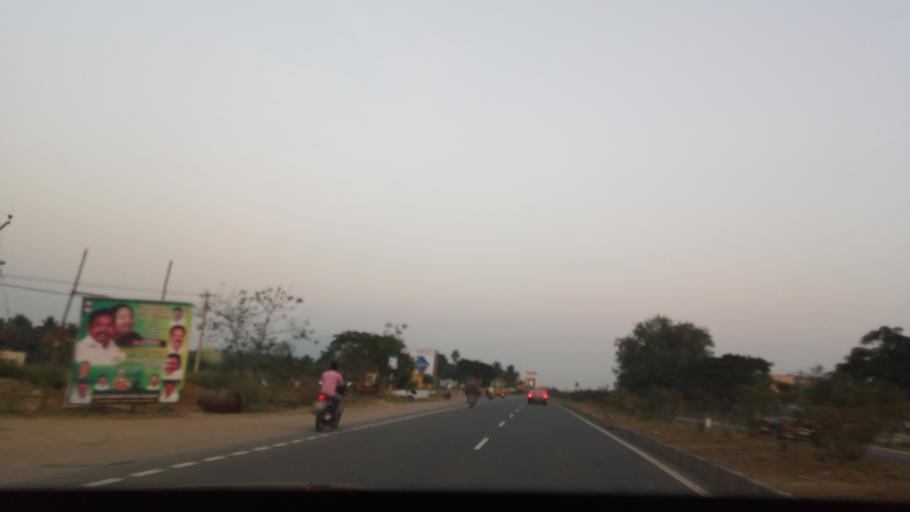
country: IN
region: Tamil Nadu
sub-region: Salem
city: Salem
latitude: 11.6671
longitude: 78.2581
